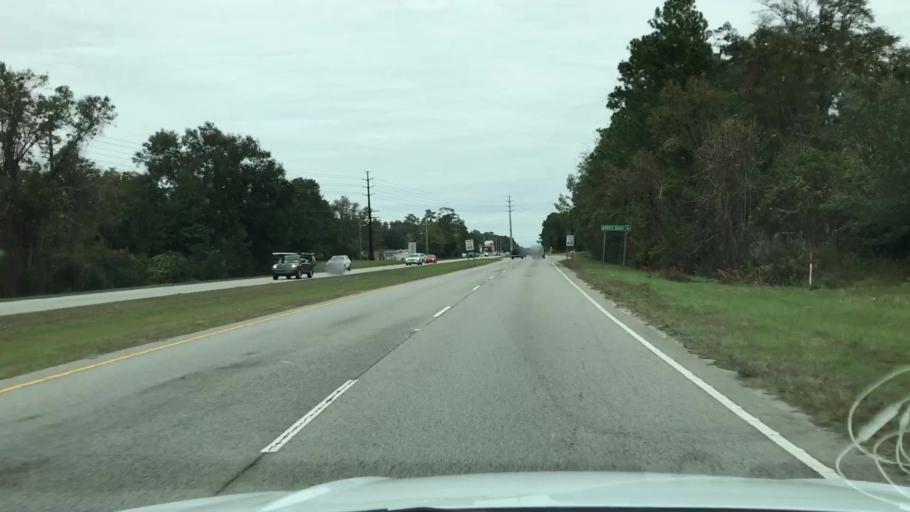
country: US
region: South Carolina
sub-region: Georgetown County
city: Murrells Inlet
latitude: 33.5304
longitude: -79.0614
